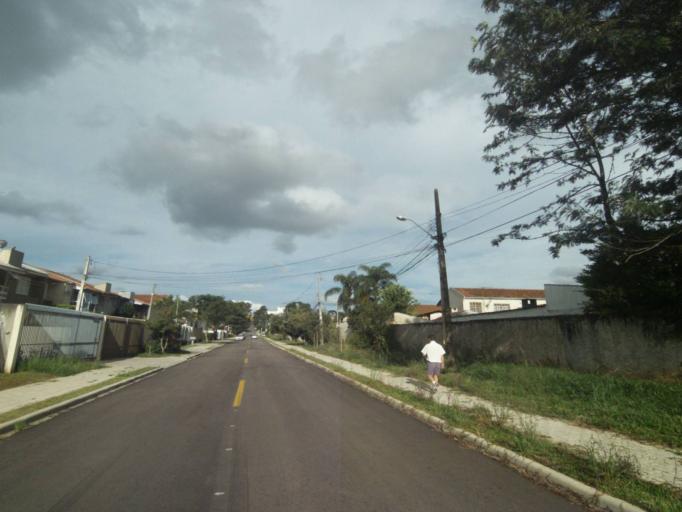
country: BR
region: Parana
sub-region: Curitiba
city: Curitiba
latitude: -25.4440
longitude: -49.3153
